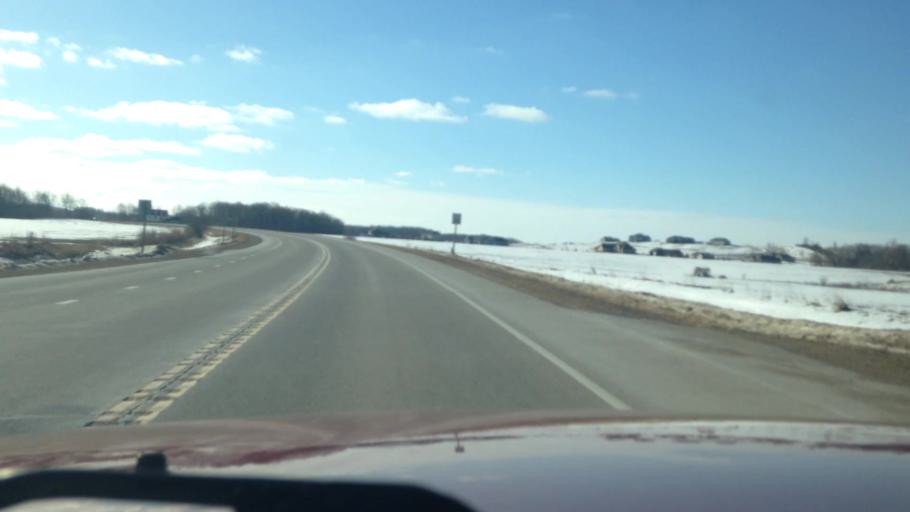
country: US
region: Wisconsin
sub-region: Waukesha County
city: Oconomowoc
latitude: 43.1786
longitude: -88.5093
